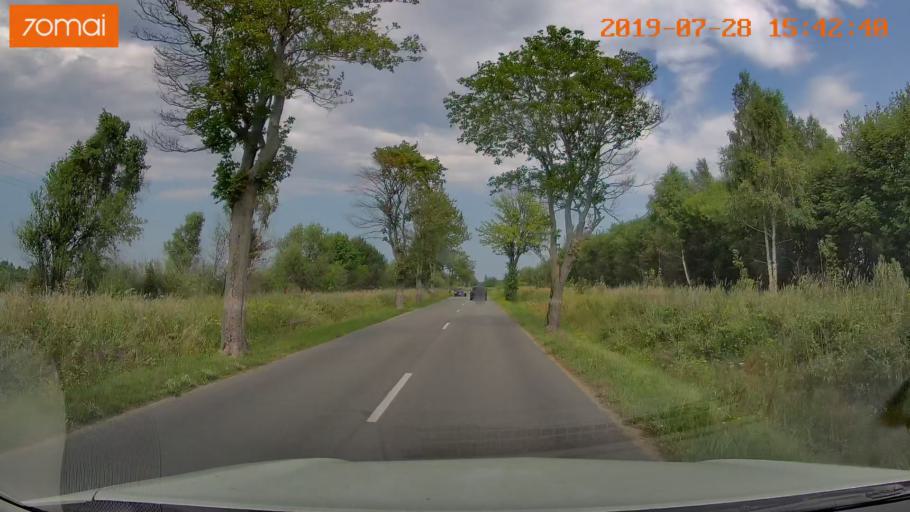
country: RU
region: Kaliningrad
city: Donskoye
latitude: 54.9323
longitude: 20.0143
